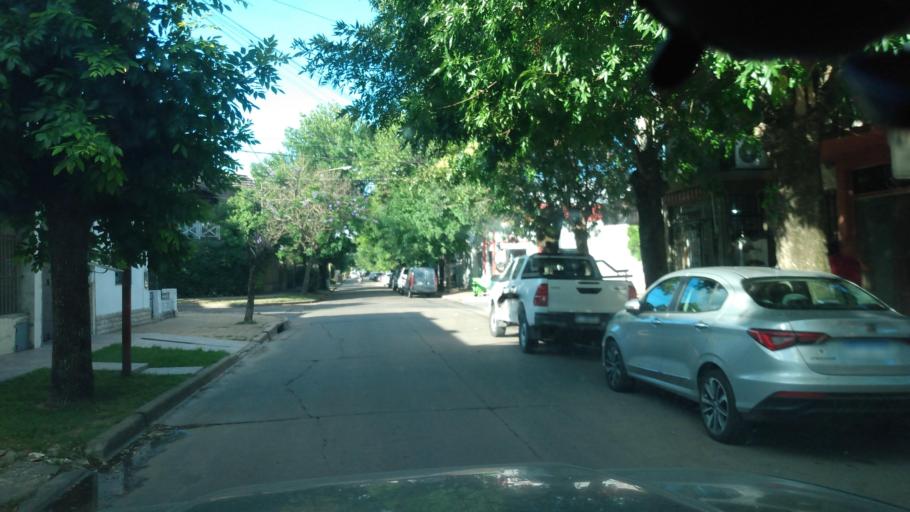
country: AR
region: Buenos Aires
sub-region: Partido de Lujan
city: Lujan
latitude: -34.5649
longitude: -59.1063
